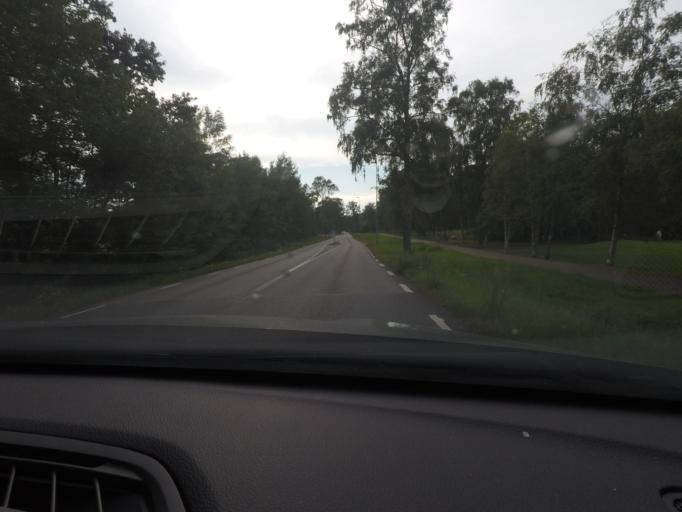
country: SE
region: Halland
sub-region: Halmstads Kommun
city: Mjallby
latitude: 56.6550
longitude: 12.7517
